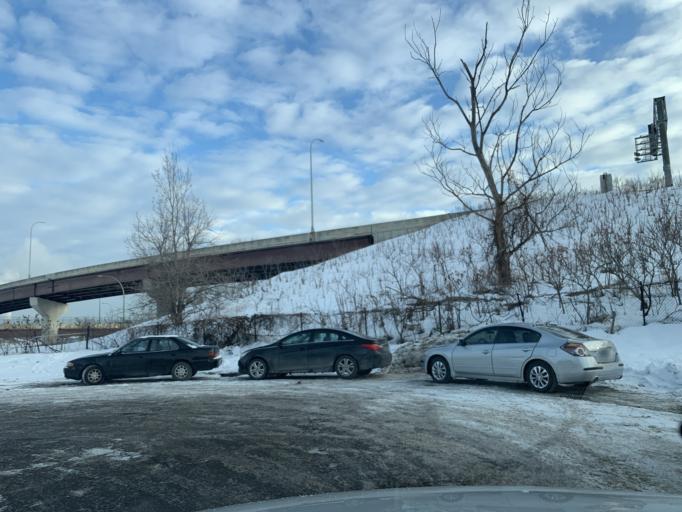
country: US
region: Minnesota
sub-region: Hennepin County
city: Minneapolis
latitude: 44.9906
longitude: -93.2854
